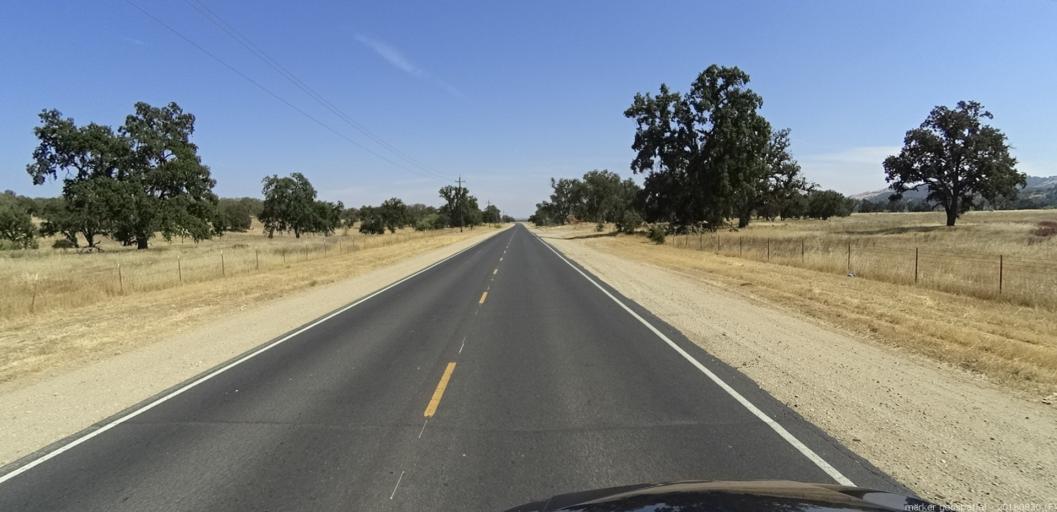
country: US
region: California
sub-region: Monterey County
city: King City
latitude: 35.9781
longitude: -121.2146
